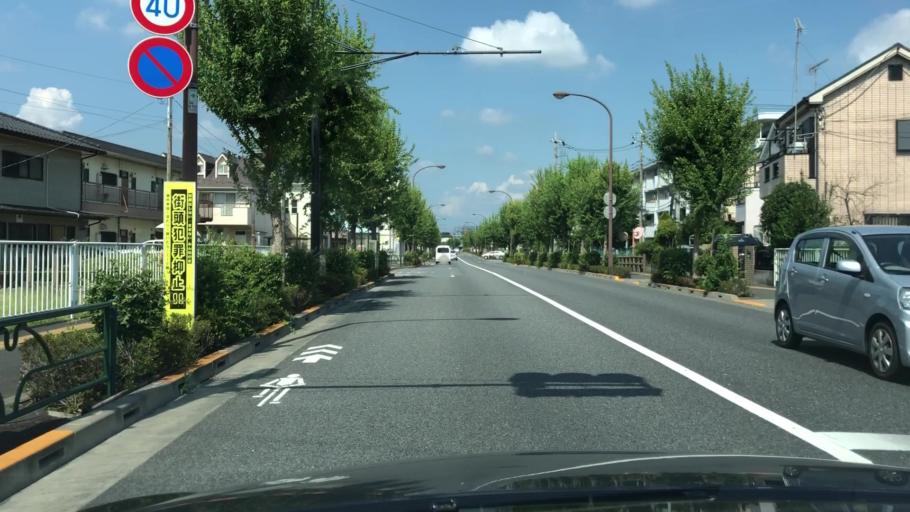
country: JP
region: Tokyo
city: Hino
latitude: 35.6831
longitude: 139.3929
